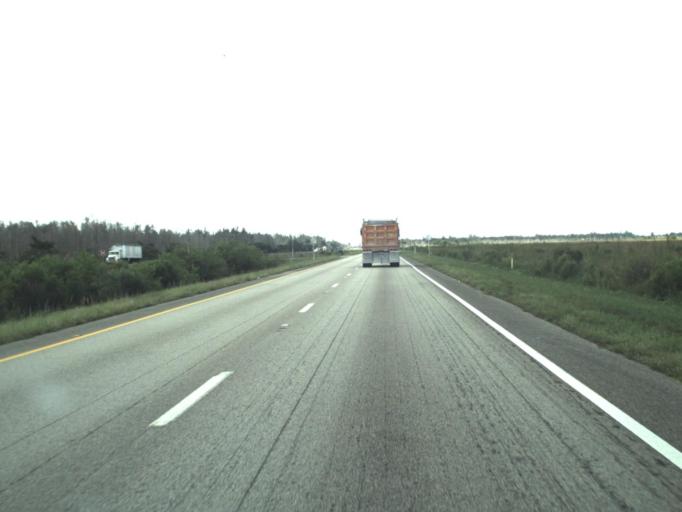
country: US
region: Florida
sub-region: Miami-Dade County
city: Palm Springs North
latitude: 25.9657
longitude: -80.4316
